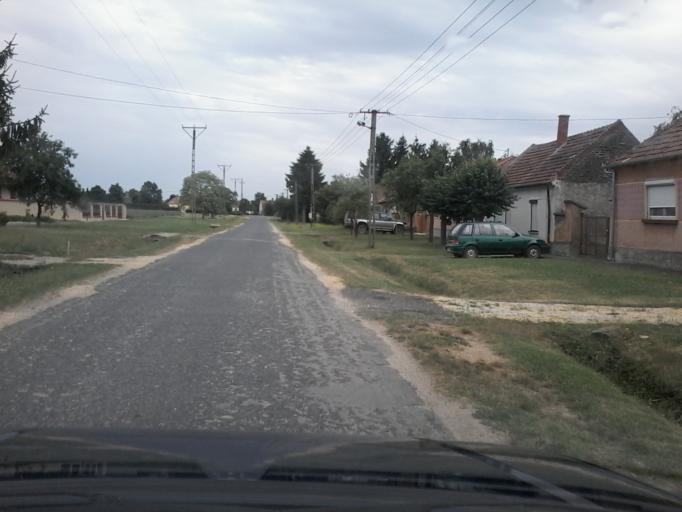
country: HU
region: Vas
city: Celldomolk
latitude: 47.2090
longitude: 17.0593
